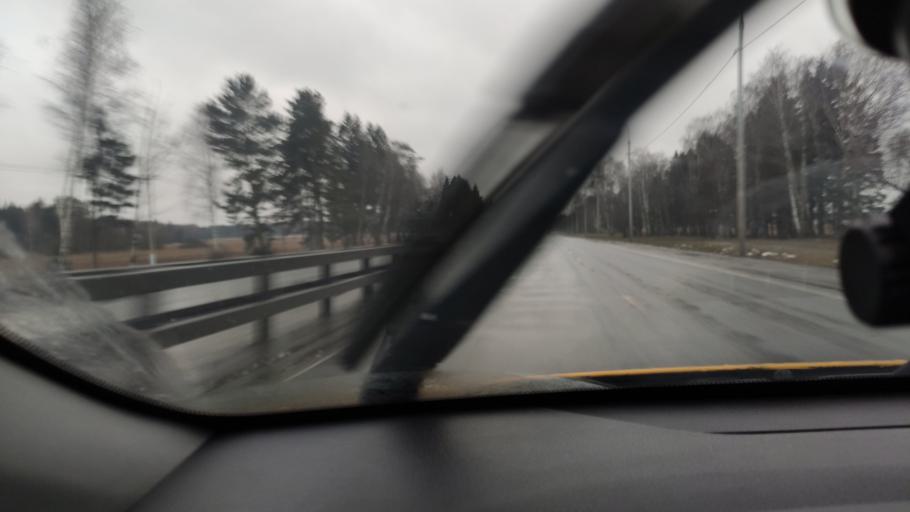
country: RU
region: Moskovskaya
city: Troitsk
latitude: 55.3397
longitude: 37.3064
